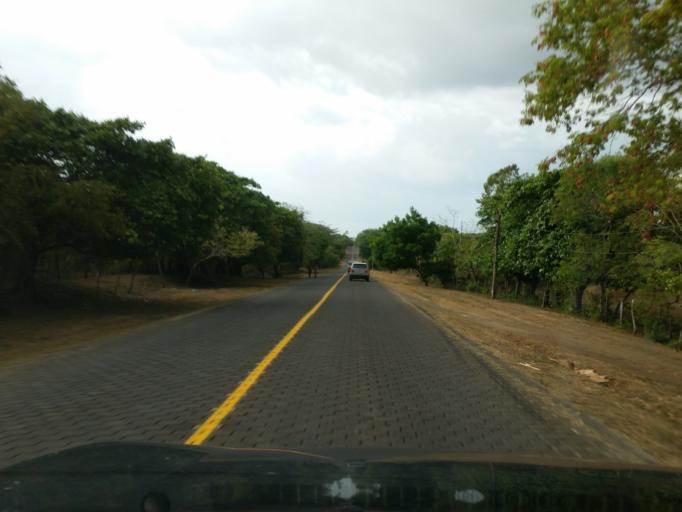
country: NI
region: Managua
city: Carlos Fonseca Amador
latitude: 11.9739
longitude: -86.5142
